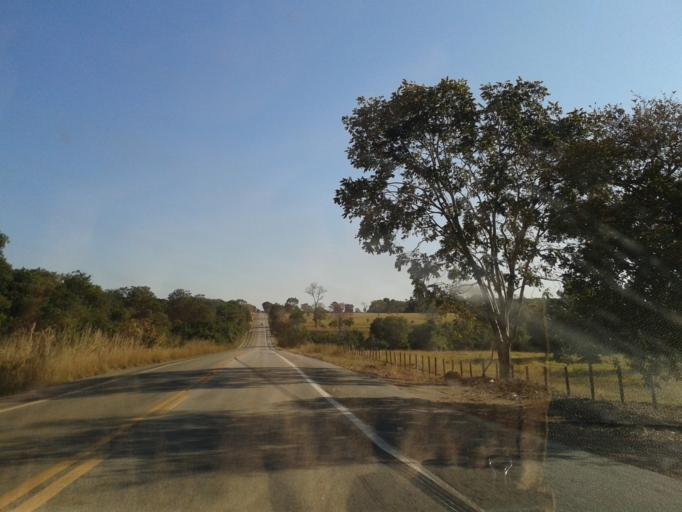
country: BR
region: Goias
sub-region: Mozarlandia
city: Mozarlandia
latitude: -15.1183
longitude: -50.6049
